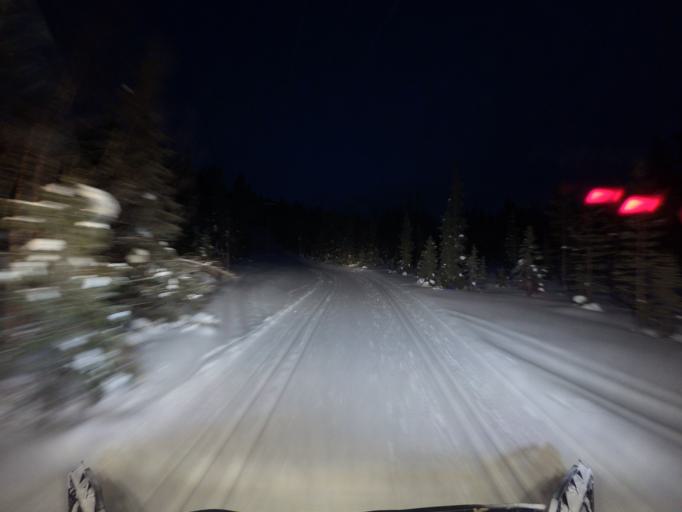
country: FI
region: Lapland
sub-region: Tunturi-Lappi
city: Kolari
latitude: 67.5816
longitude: 24.0787
